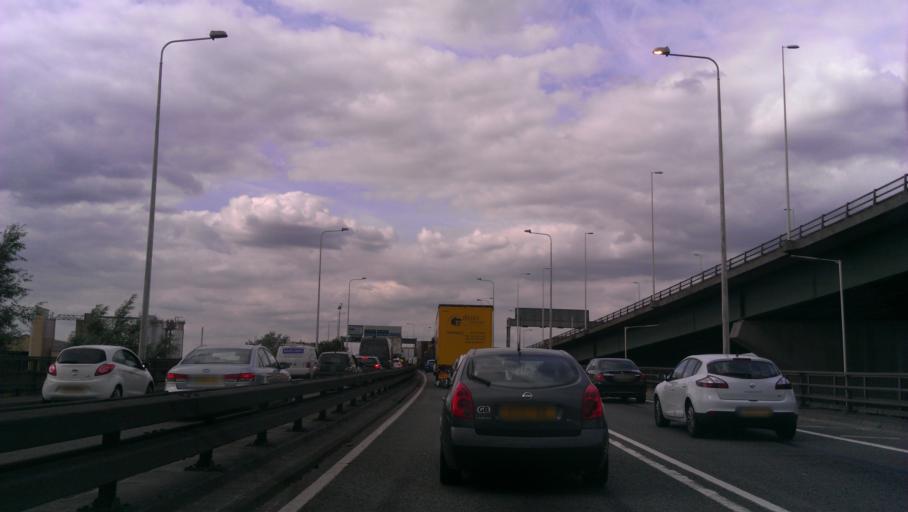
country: GB
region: England
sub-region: Kent
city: West Thurrock
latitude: 51.4754
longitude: 0.2659
